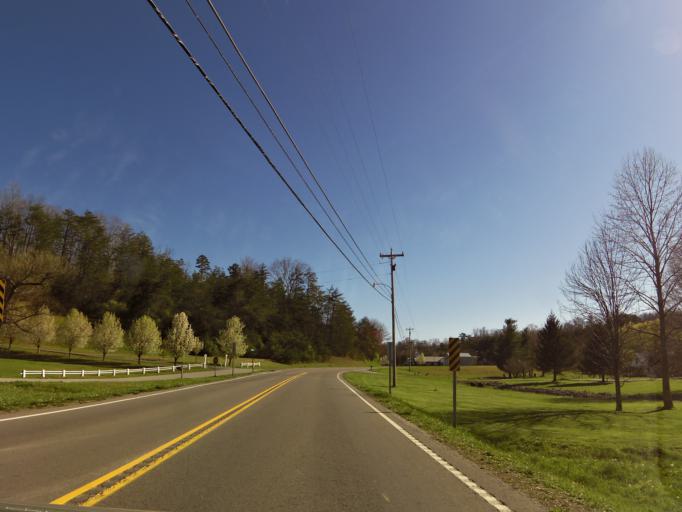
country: US
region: Tennessee
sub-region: Scott County
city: Oneida
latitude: 36.4888
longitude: -84.5068
